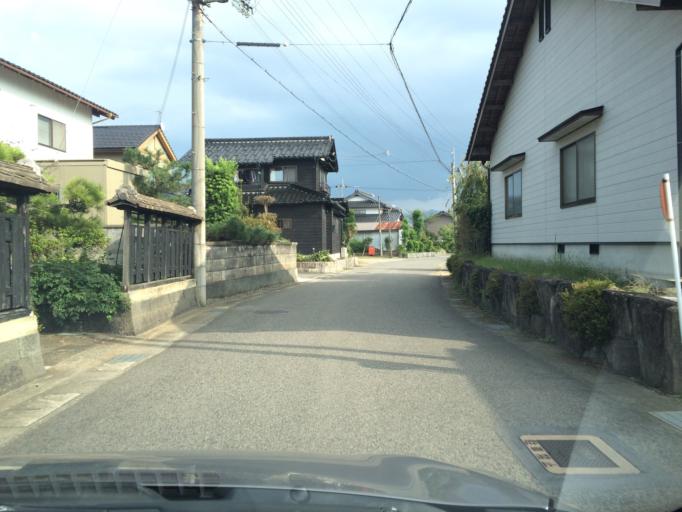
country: JP
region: Hyogo
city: Toyooka
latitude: 35.5235
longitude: 134.8267
